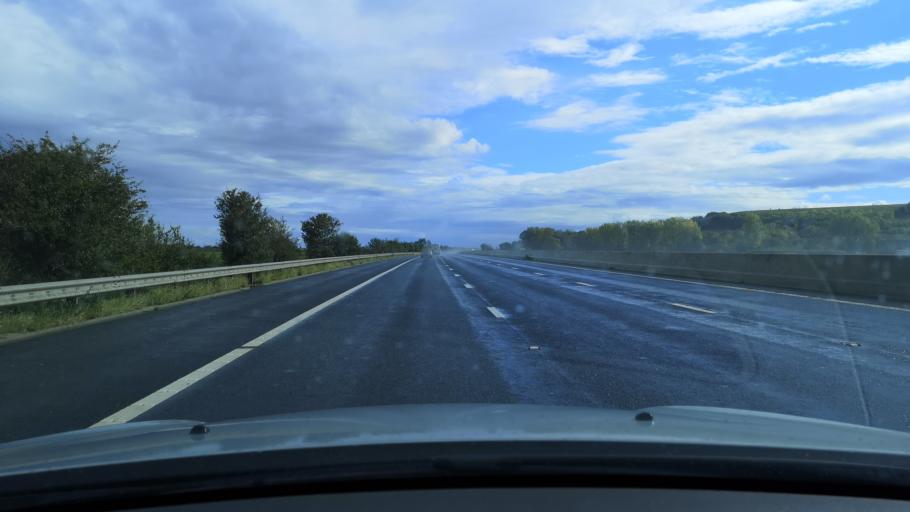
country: GB
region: England
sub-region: City and Borough of Wakefield
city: Knottingley
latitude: 53.6953
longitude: -1.1949
